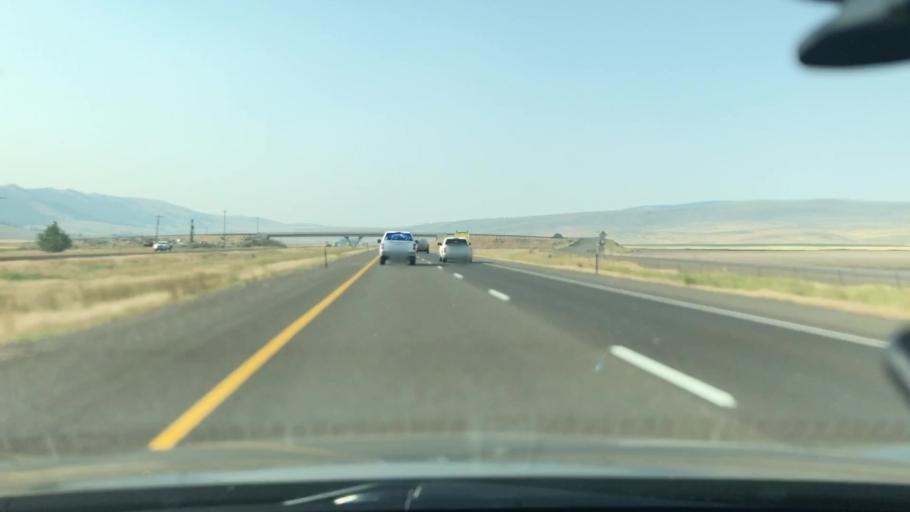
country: US
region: Oregon
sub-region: Union County
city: Union
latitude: 45.0936
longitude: -117.9517
